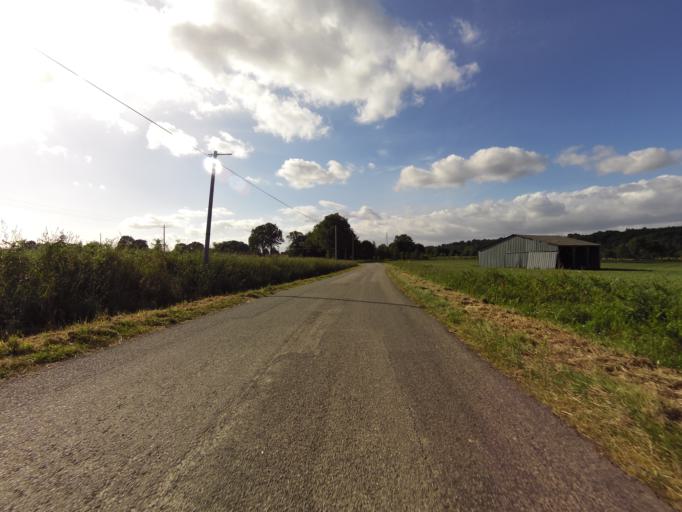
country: FR
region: Brittany
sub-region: Departement du Morbihan
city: Molac
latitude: 47.7115
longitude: -2.4082
